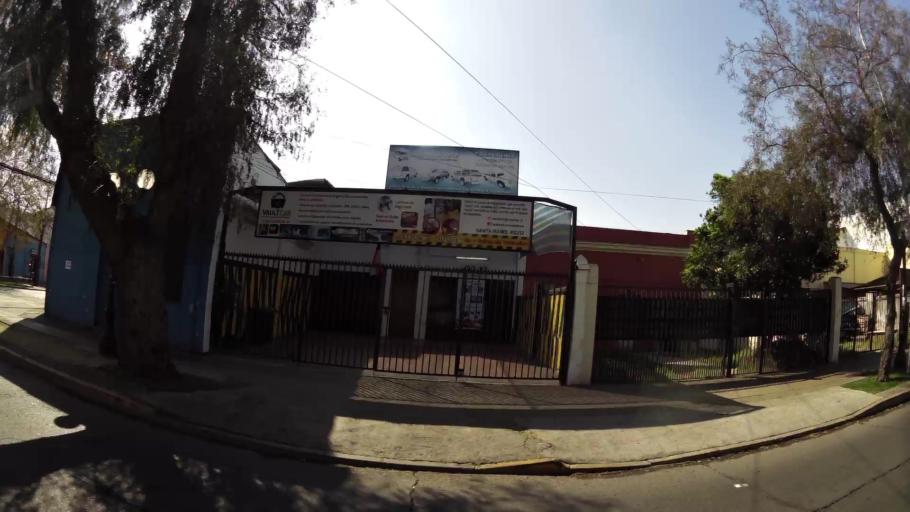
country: CL
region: Santiago Metropolitan
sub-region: Provincia de Santiago
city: Santiago
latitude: -33.4469
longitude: -70.6282
